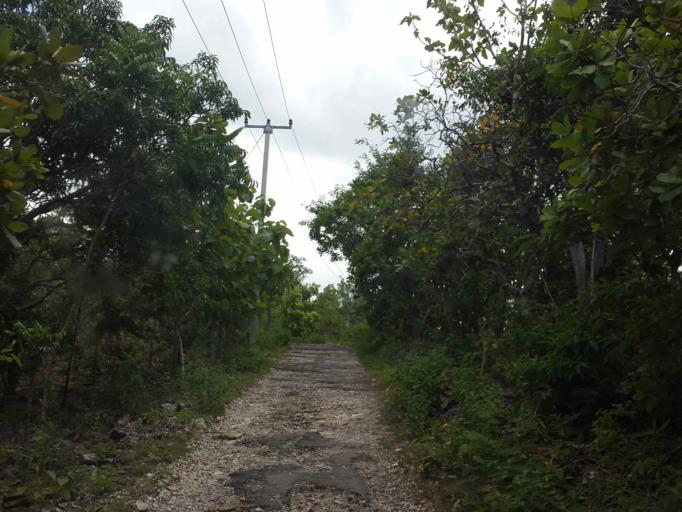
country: ID
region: Bali
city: Klumbu
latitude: -8.7154
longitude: 115.5232
